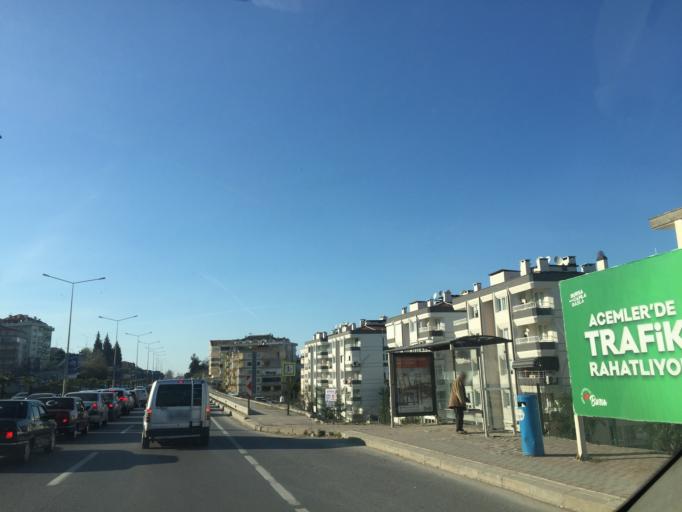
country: TR
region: Bursa
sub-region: Mudanya
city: Mudanya
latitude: 40.3589
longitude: 28.9117
